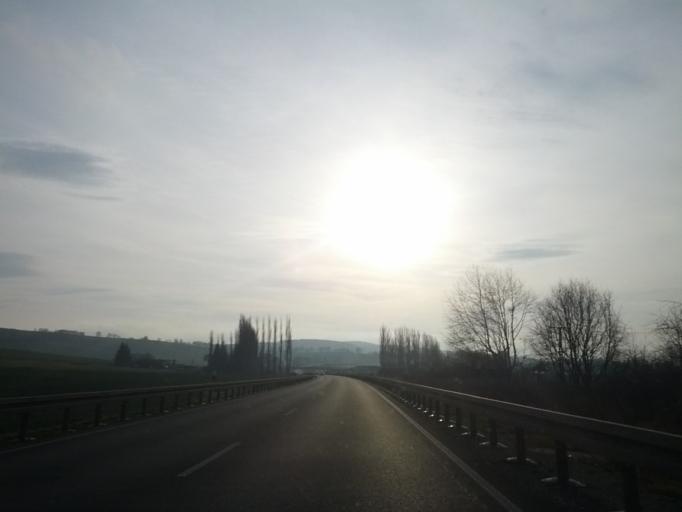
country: DE
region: Thuringia
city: Fambach
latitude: 50.7341
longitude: 10.3616
